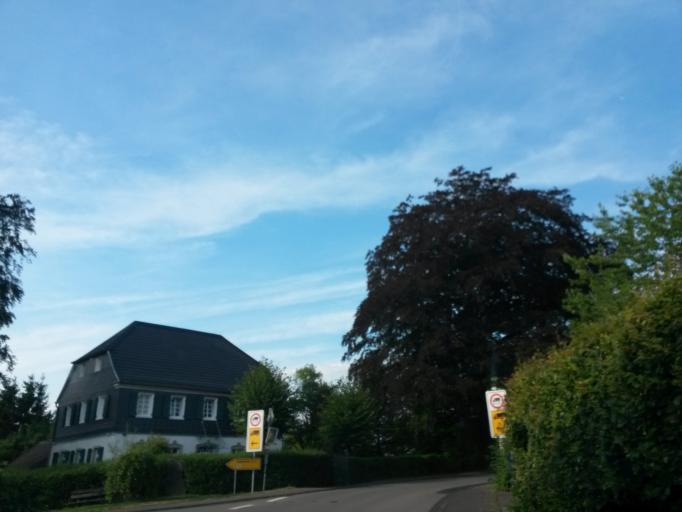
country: DE
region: North Rhine-Westphalia
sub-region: Regierungsbezirk Koln
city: Overath
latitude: 50.9799
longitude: 7.3099
